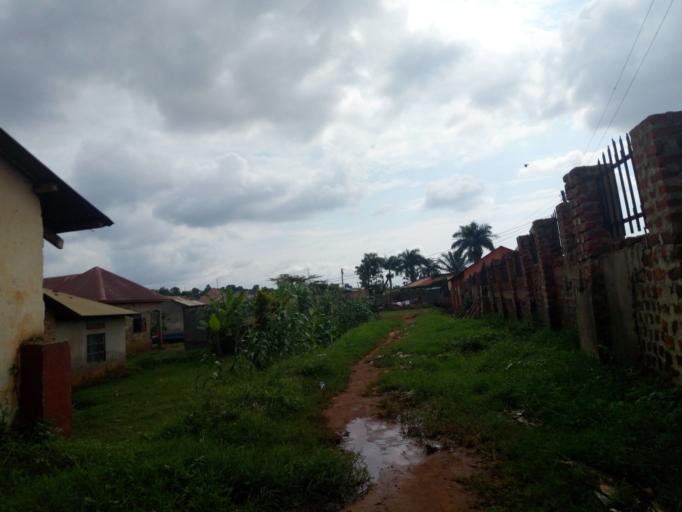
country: UG
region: Central Region
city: Kampala Central Division
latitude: 0.3456
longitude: 32.5585
